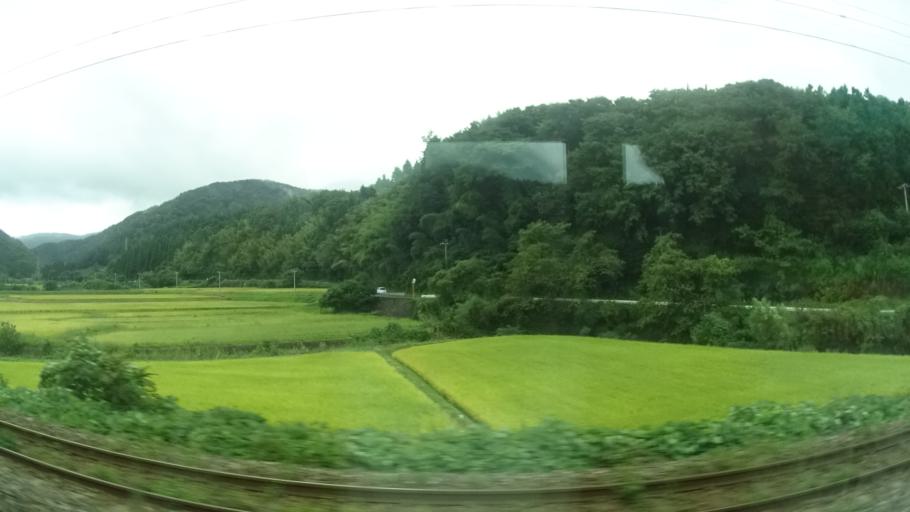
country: JP
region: Yamagata
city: Tsuruoka
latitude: 38.7004
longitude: 139.6792
